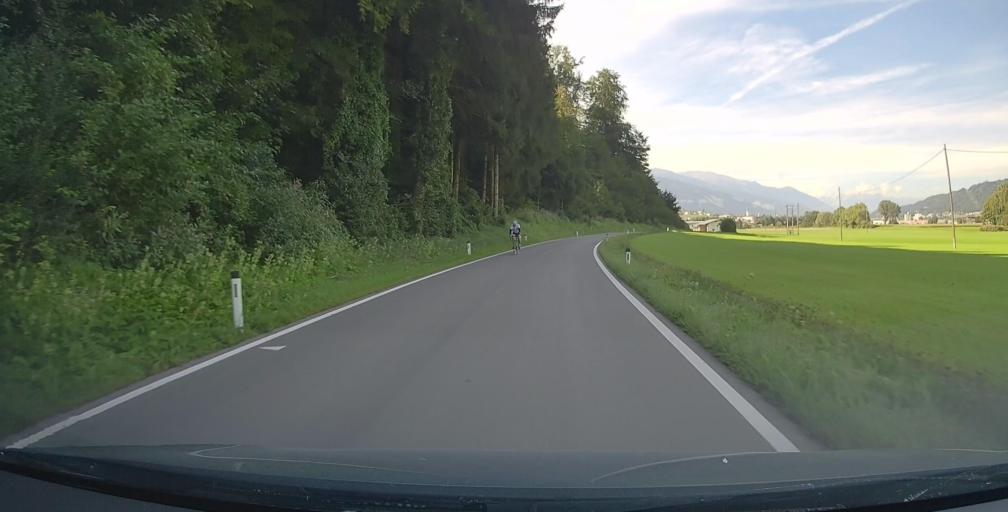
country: AT
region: Tyrol
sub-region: Politischer Bezirk Schwaz
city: Buch bei Jenbach
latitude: 47.3639
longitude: 11.7378
